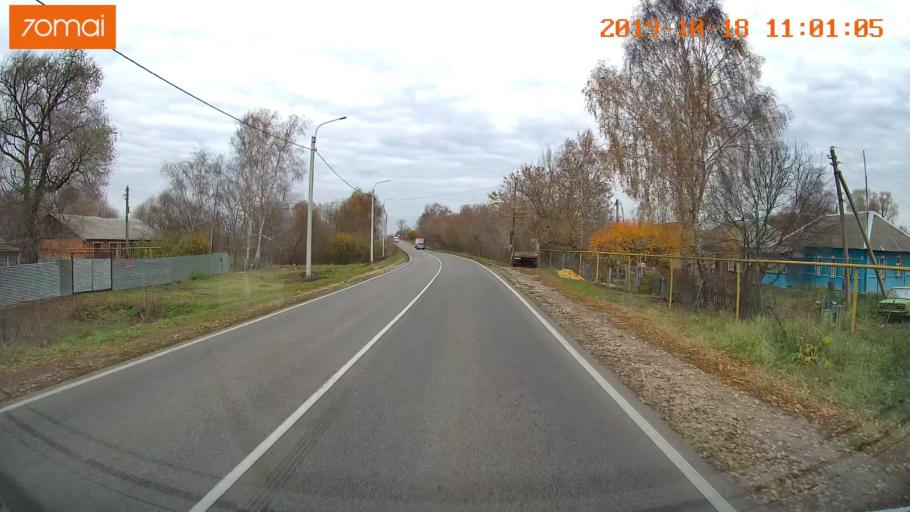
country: RU
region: Tula
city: Yepifan'
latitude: 53.8506
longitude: 38.5527
